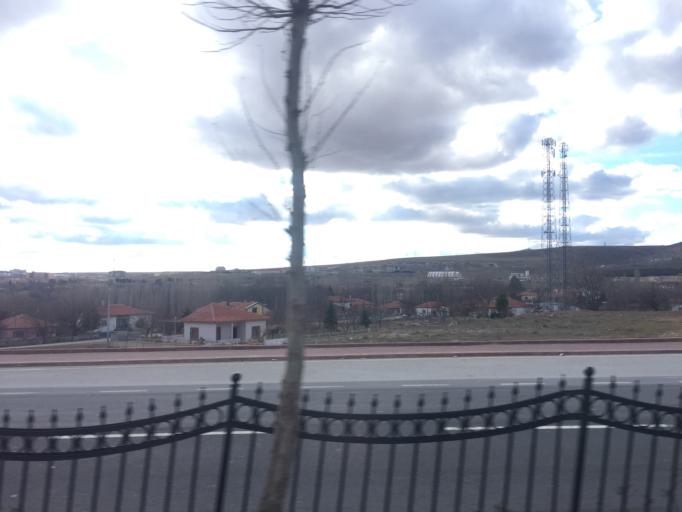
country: TR
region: Kirsehir
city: Kirsehir
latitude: 39.1692
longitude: 34.1510
